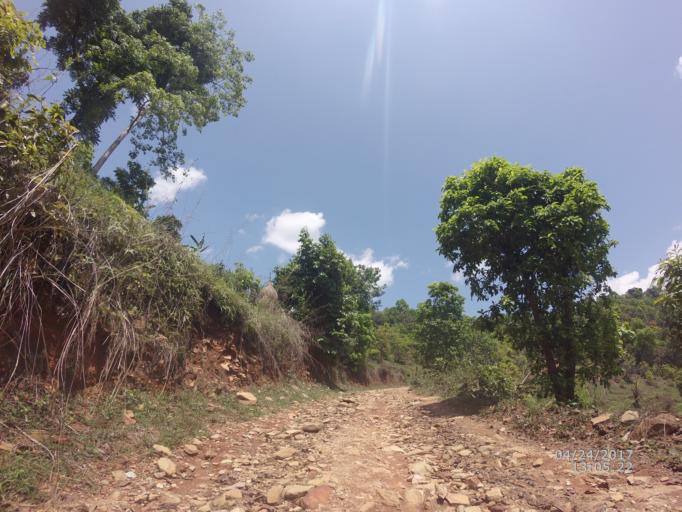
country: NP
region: Western Region
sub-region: Gandaki Zone
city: Pokhara
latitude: 28.1876
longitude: 84.0975
